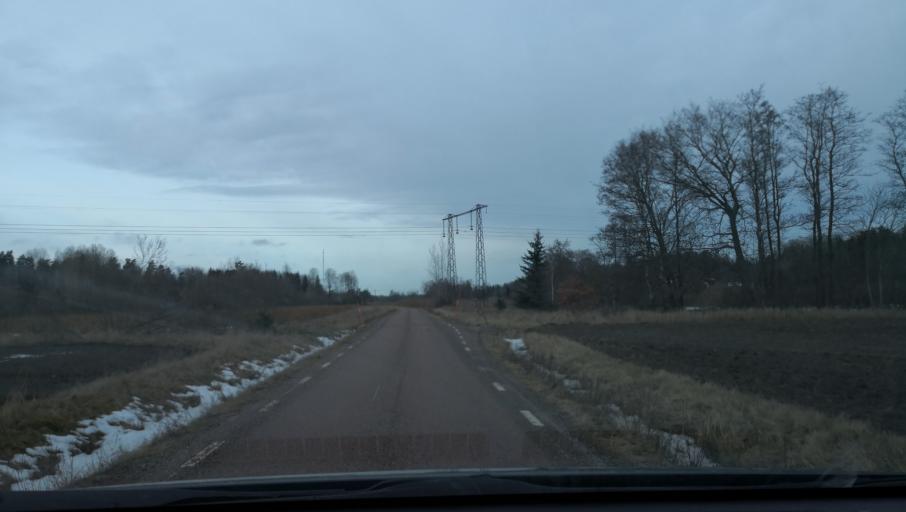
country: SE
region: Vaestmanland
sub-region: Vasteras
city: Skultuna
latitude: 59.6064
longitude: 16.4118
